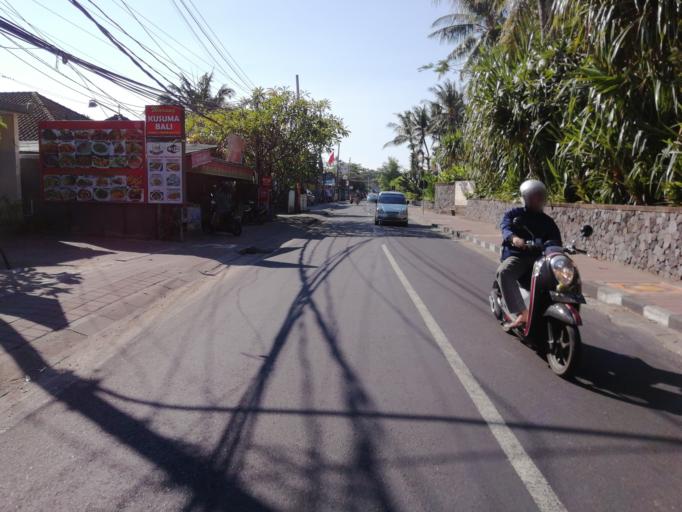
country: ID
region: Bali
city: Bualu
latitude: -8.7816
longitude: 115.2244
